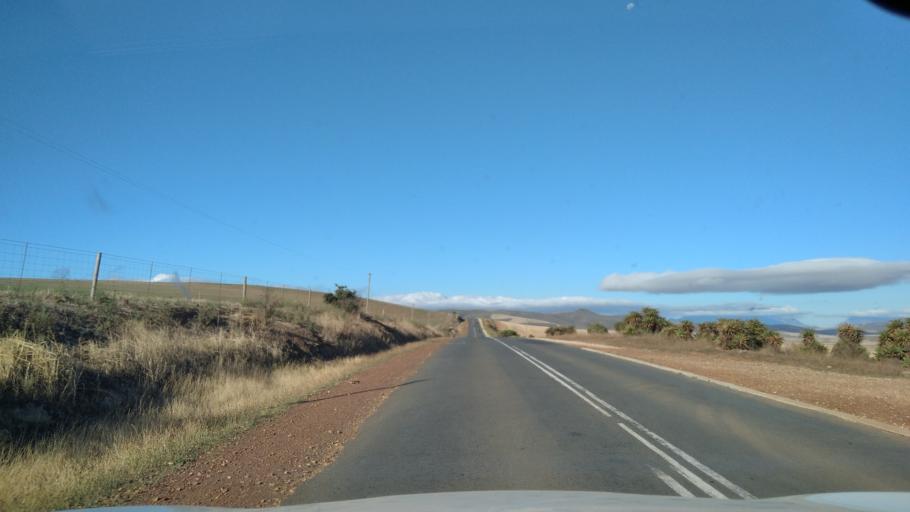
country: ZA
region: Western Cape
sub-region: Overberg District Municipality
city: Caledon
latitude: -34.1856
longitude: 19.2726
